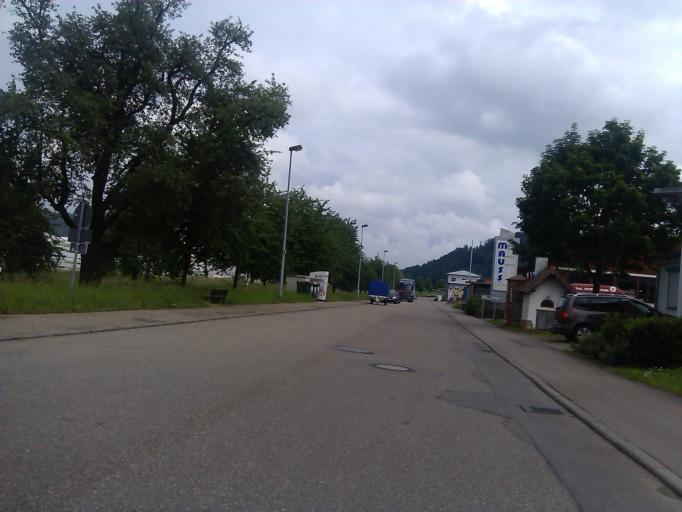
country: DE
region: Baden-Wuerttemberg
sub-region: Regierungsbezirk Stuttgart
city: Gaildorf
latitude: 48.9783
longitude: 9.7820
